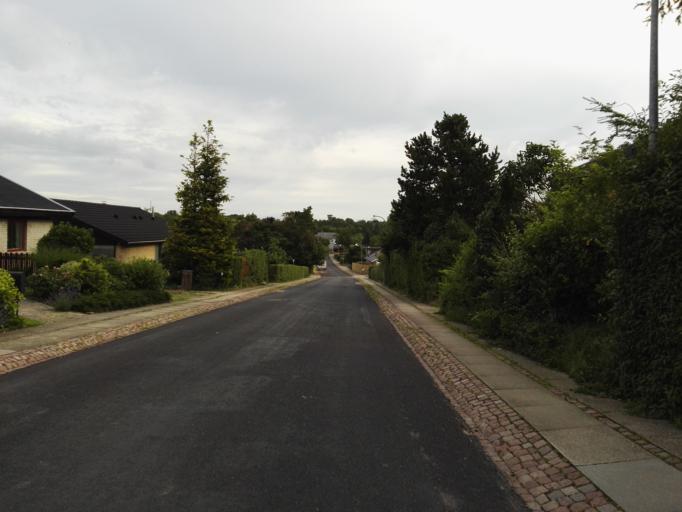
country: DK
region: Capital Region
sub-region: Ballerup Kommune
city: Malov
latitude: 55.7562
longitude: 12.3200
